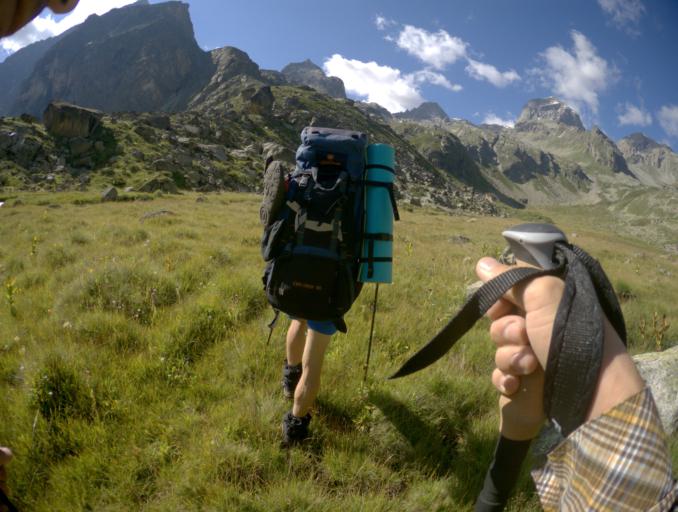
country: RU
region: Karachayevo-Cherkesiya
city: Uchkulan
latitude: 43.3326
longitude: 42.1150
